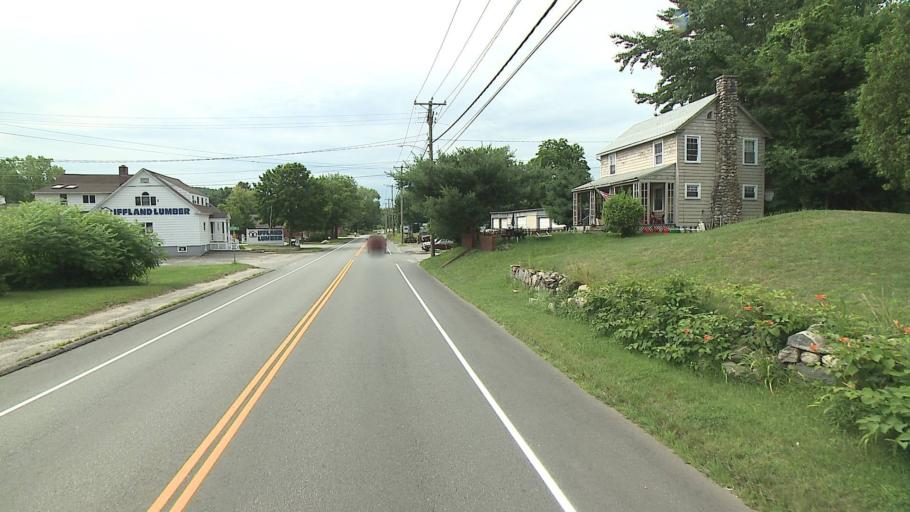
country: US
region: Connecticut
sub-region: Litchfield County
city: Torrington
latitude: 41.7859
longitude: -73.1174
